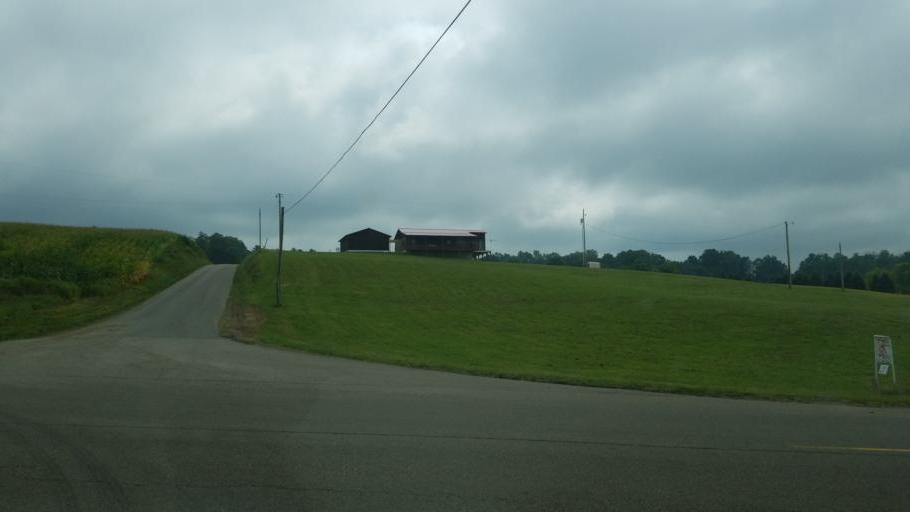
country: US
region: Ohio
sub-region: Licking County
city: Utica
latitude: 40.2527
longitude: -82.4092
